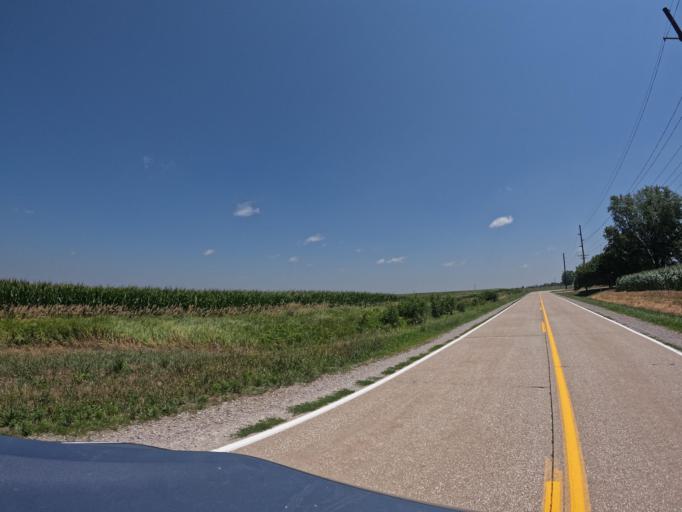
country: US
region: Iowa
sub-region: Keokuk County
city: Sigourney
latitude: 41.2758
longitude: -92.1631
